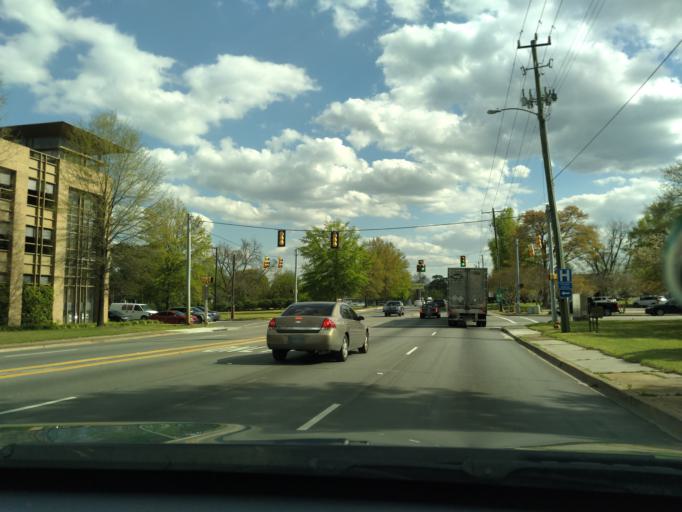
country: US
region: South Carolina
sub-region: Florence County
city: Florence
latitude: 34.1963
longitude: -79.7620
